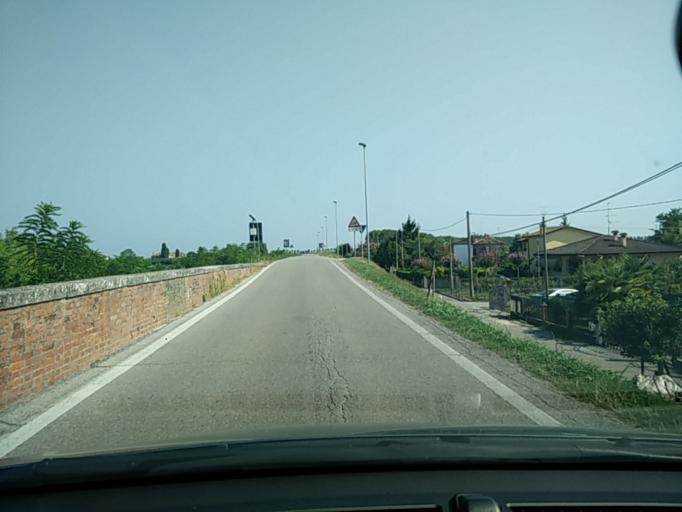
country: IT
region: Veneto
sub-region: Provincia di Venezia
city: La Salute di Livenza
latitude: 45.6479
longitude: 12.8146
